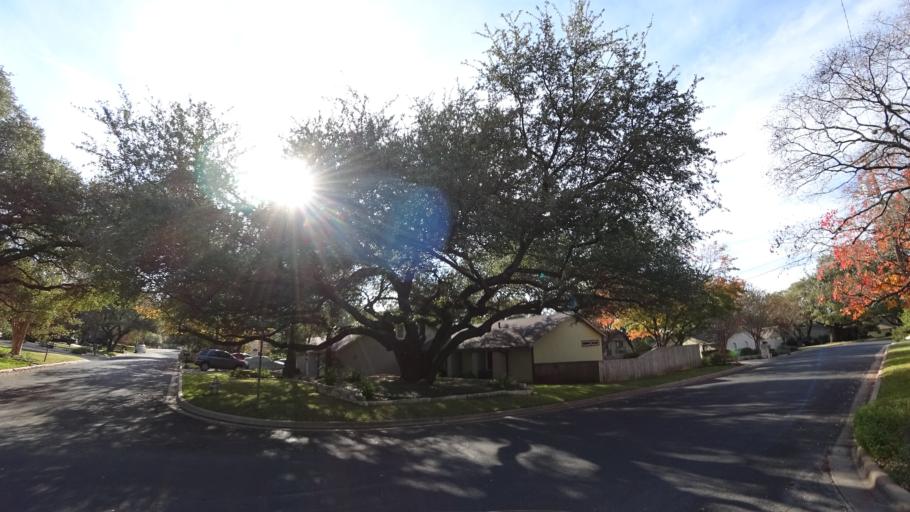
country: US
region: Texas
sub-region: Williamson County
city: Jollyville
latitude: 30.3858
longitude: -97.7485
